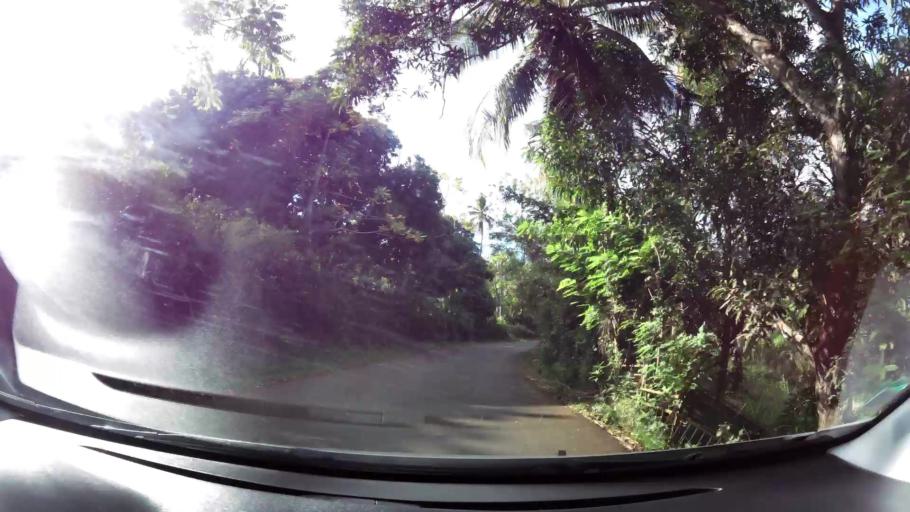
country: YT
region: Ouangani
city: Ouangani
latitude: -12.8417
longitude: 45.1322
